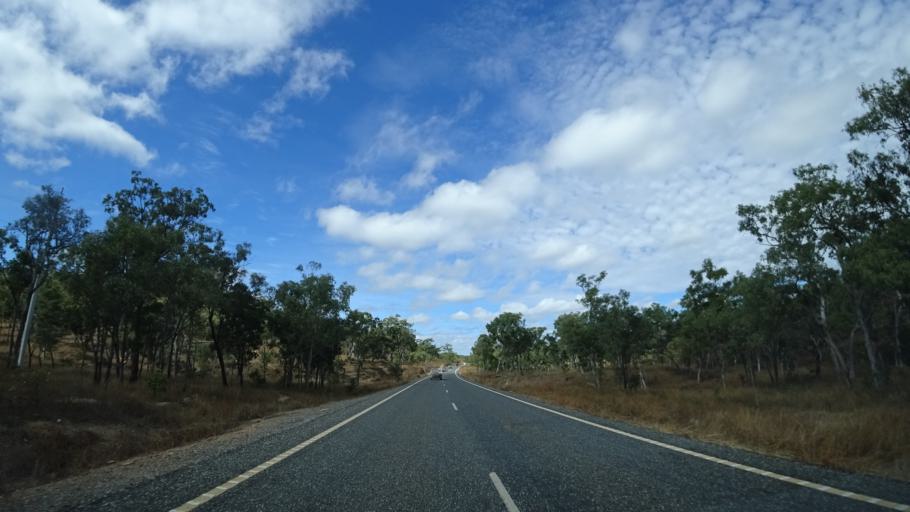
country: AU
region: Queensland
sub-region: Cairns
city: Port Douglas
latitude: -16.3058
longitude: 144.7166
